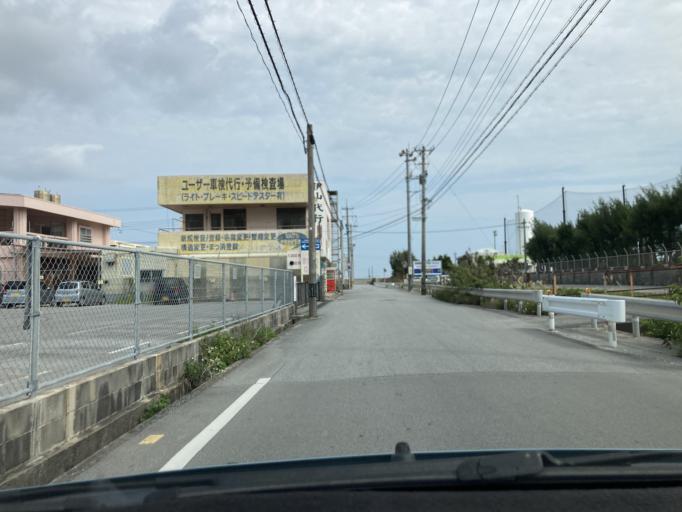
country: JP
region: Okinawa
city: Ginowan
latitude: 26.2716
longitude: 127.7152
